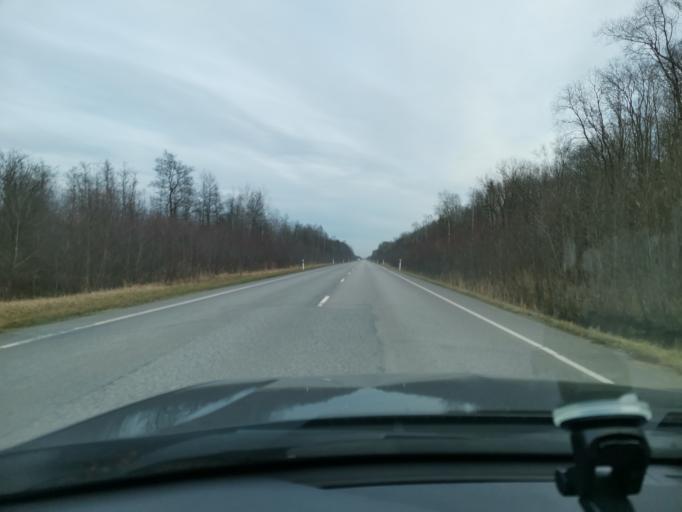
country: EE
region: Ida-Virumaa
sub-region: Narva-Joesuu linn
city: Narva-Joesuu
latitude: 59.3289
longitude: 27.9386
